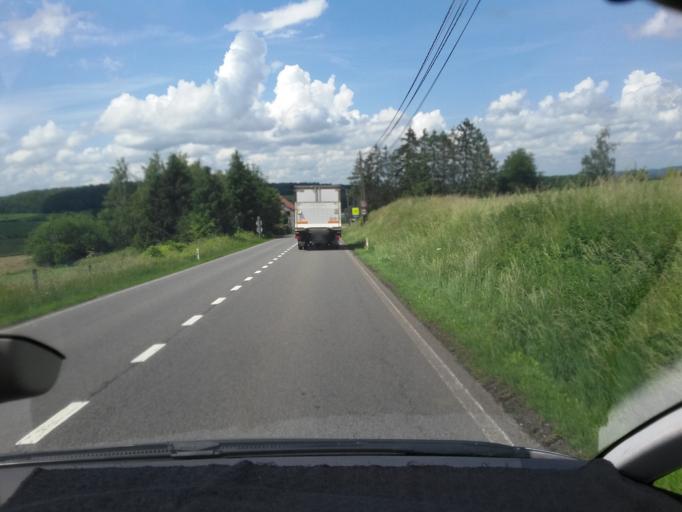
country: BE
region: Wallonia
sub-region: Province de Namur
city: Rochefort
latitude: 50.1390
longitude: 5.2242
